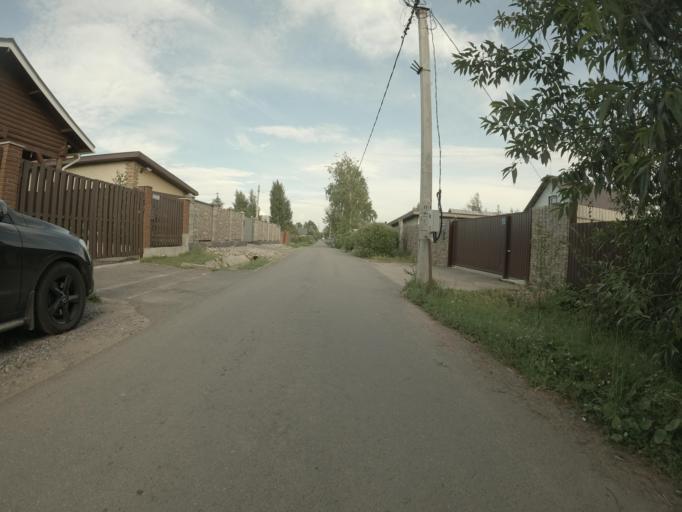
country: RU
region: St.-Petersburg
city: Krasnogvargeisky
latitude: 59.9378
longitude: 30.5102
